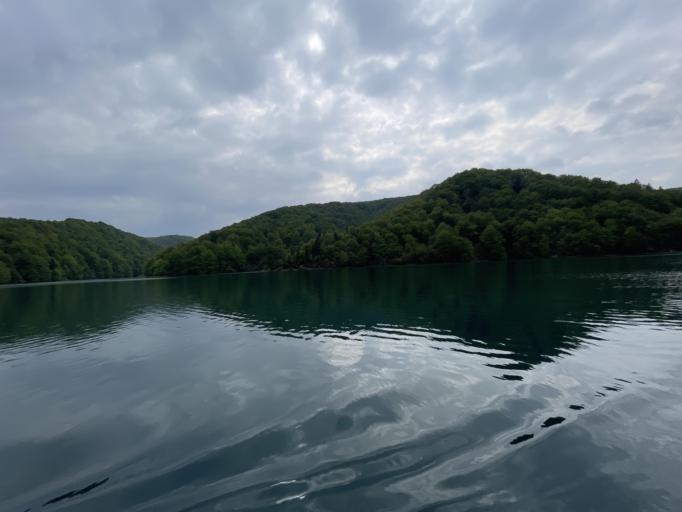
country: HR
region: Licko-Senjska
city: Jezerce
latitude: 44.8892
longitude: 15.6065
